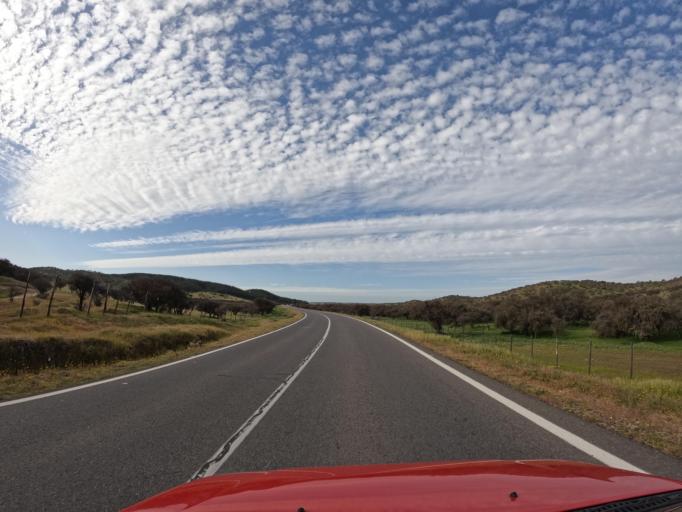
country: CL
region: O'Higgins
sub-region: Provincia de Colchagua
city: Santa Cruz
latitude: -34.3115
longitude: -71.7380
